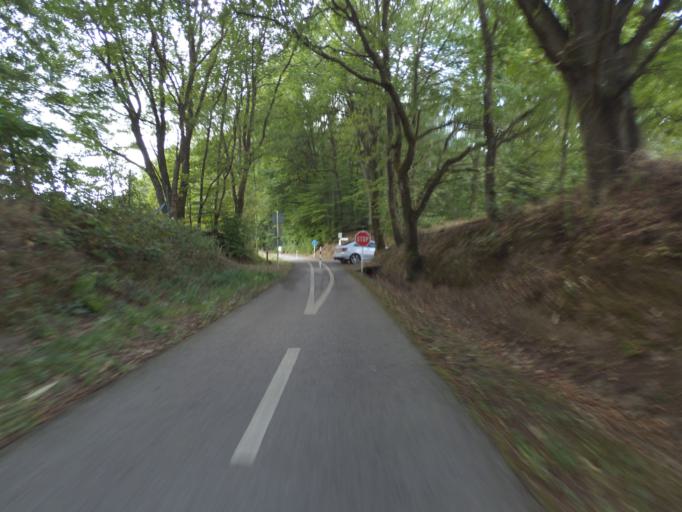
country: LU
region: Grevenmacher
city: Gonderange
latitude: 49.6710
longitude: 6.2332
